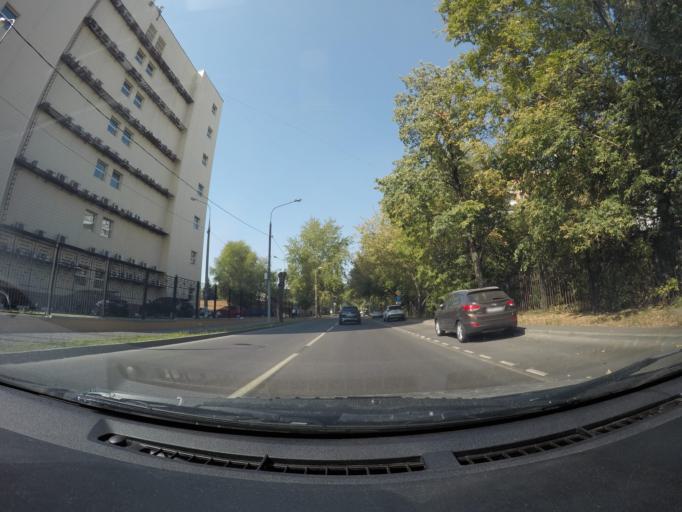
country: RU
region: Moscow
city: Sokol'niki
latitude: 55.7874
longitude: 37.6715
